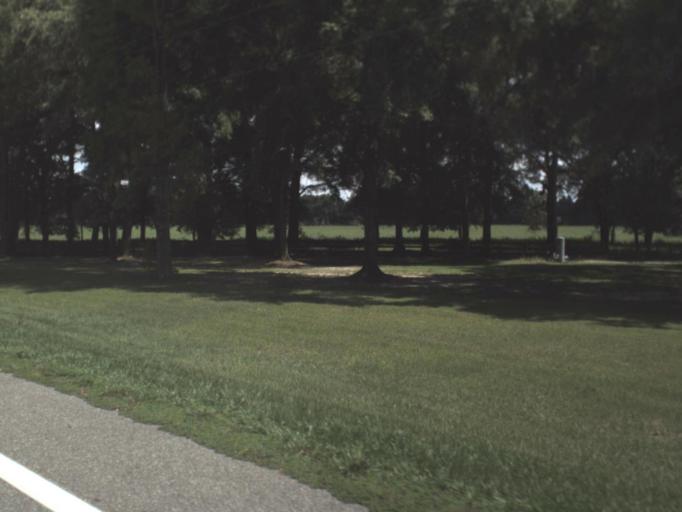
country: US
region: Florida
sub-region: Lafayette County
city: Mayo
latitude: 30.0253
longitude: -83.0529
